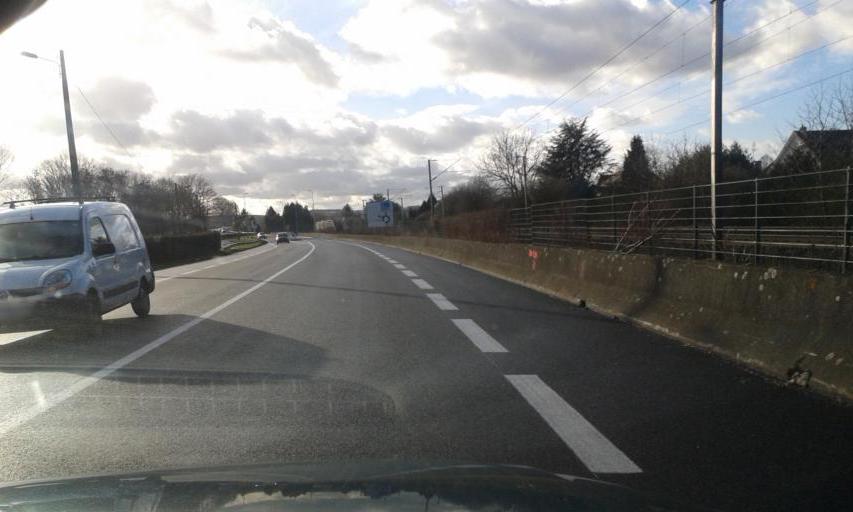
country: FR
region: Picardie
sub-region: Departement de l'Oise
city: Venette
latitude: 49.4129
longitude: 2.8003
